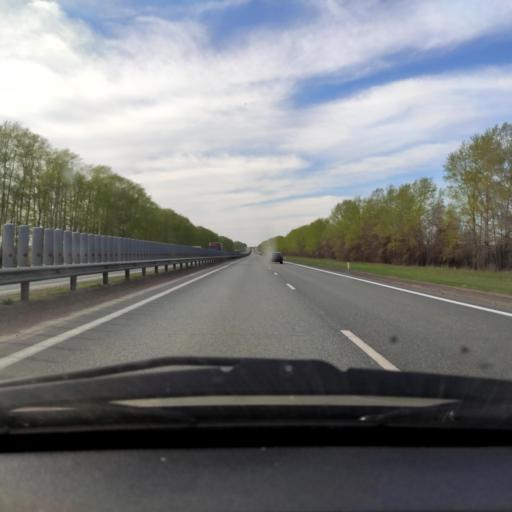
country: RU
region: Bashkortostan
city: Asanovo
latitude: 55.0169
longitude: 55.4771
